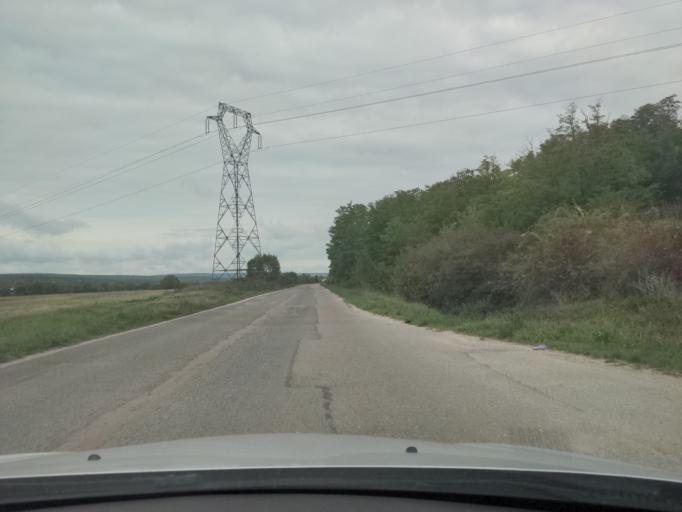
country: FR
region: Bourgogne
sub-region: Departement de la Cote-d'Or
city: Ahuy
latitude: 47.3595
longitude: 5.0389
